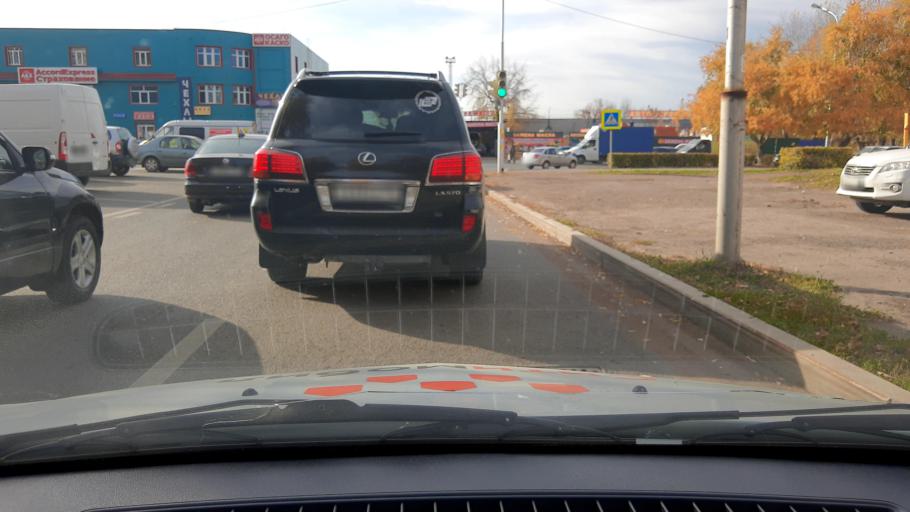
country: RU
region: Bashkortostan
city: Ufa
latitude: 54.8083
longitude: 56.0983
